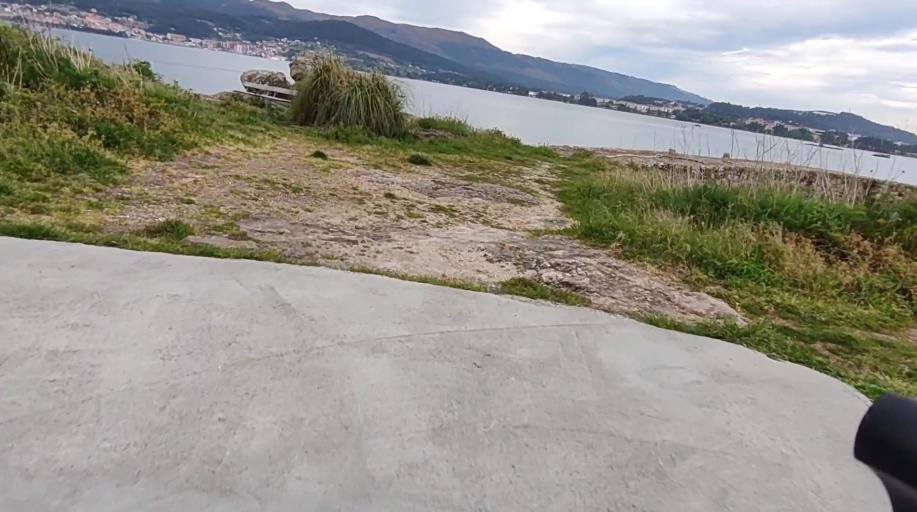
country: ES
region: Galicia
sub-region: Provincia da Coruna
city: Boiro
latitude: 42.6258
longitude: -8.8826
